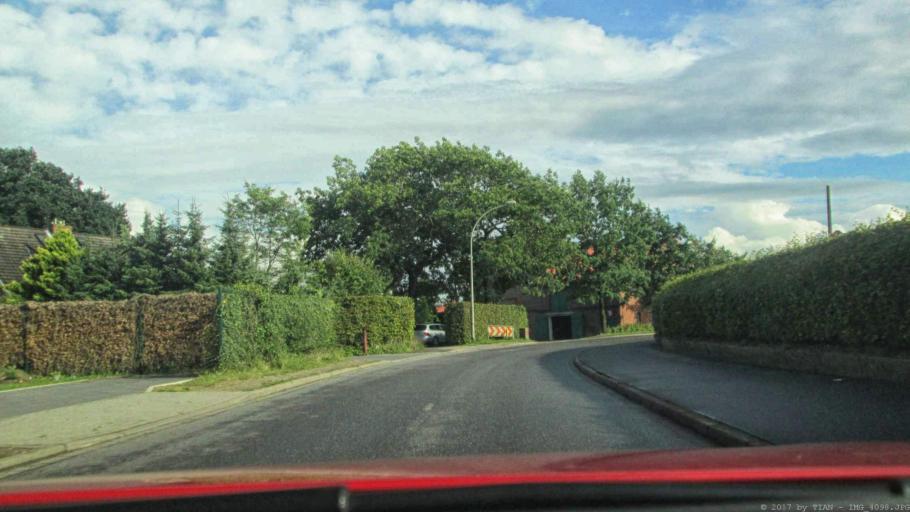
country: DE
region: Schleswig-Holstein
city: Rellingen
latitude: 53.6387
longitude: 9.8049
